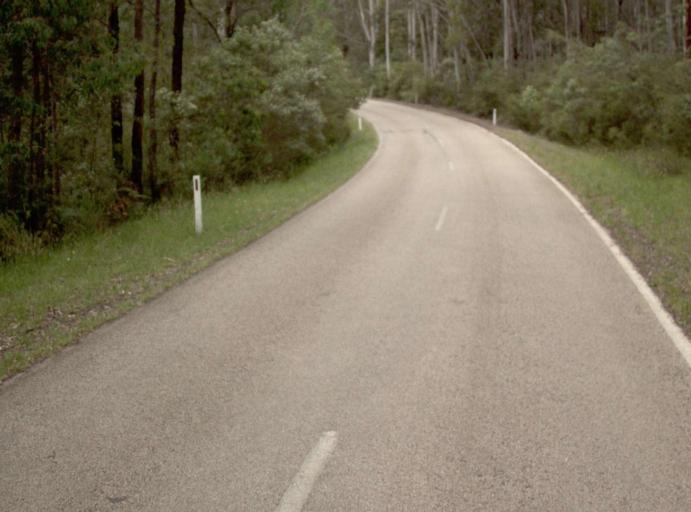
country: AU
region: Victoria
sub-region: East Gippsland
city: Bairnsdale
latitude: -37.6210
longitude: 147.1931
